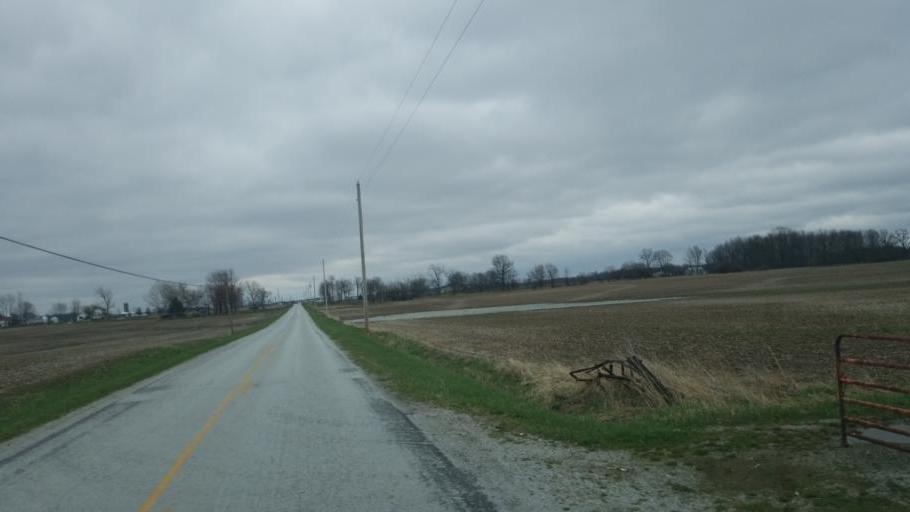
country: US
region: Ohio
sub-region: Hardin County
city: Kenton
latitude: 40.6584
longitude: -83.5462
